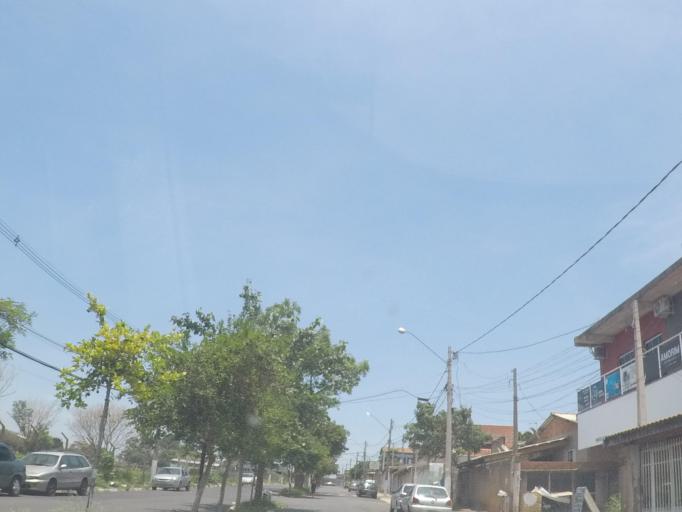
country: BR
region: Sao Paulo
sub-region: Hortolandia
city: Hortolandia
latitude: -22.8469
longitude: -47.1866
